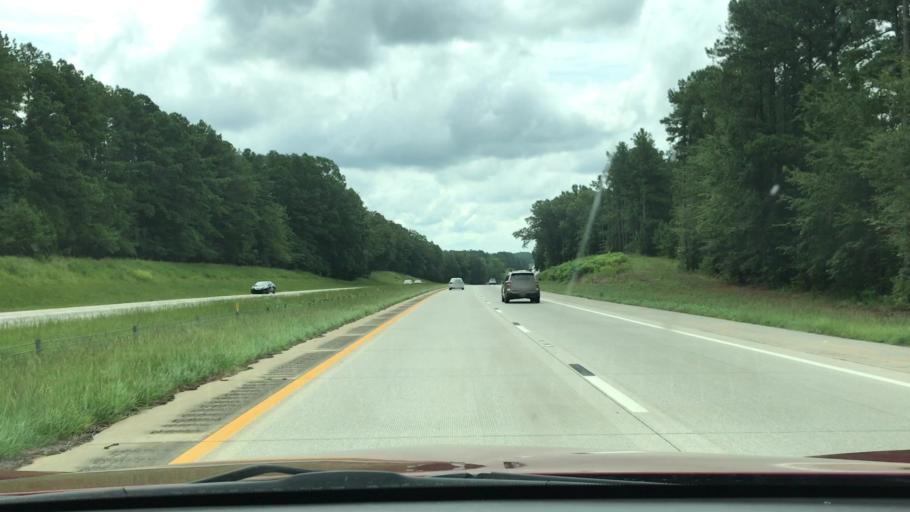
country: US
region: South Carolina
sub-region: Laurens County
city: Laurens
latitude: 34.6042
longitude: -82.0644
